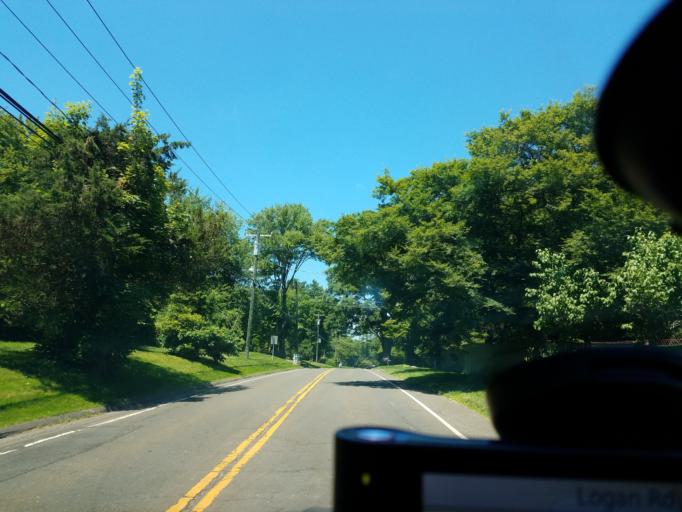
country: US
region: Connecticut
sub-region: Fairfield County
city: New Canaan
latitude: 41.1787
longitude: -73.5188
